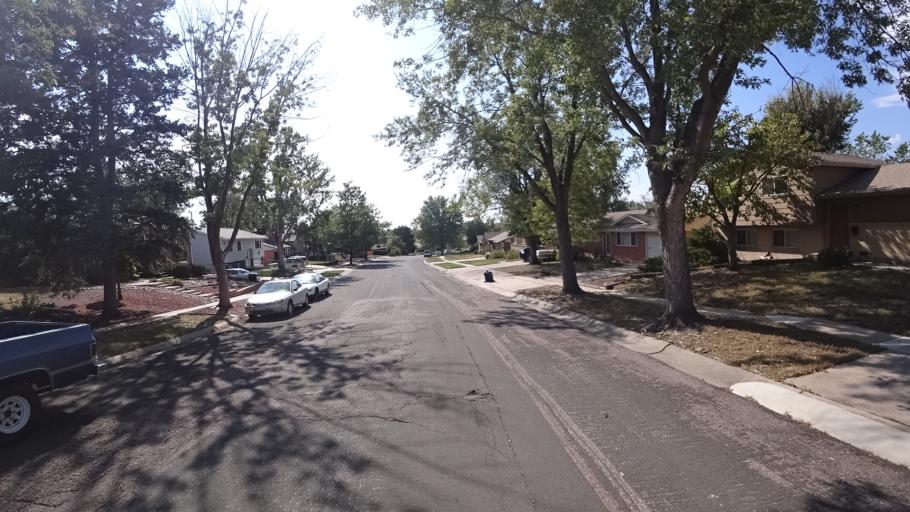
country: US
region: Colorado
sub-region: El Paso County
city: Colorado Springs
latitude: 38.8613
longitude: -104.7639
